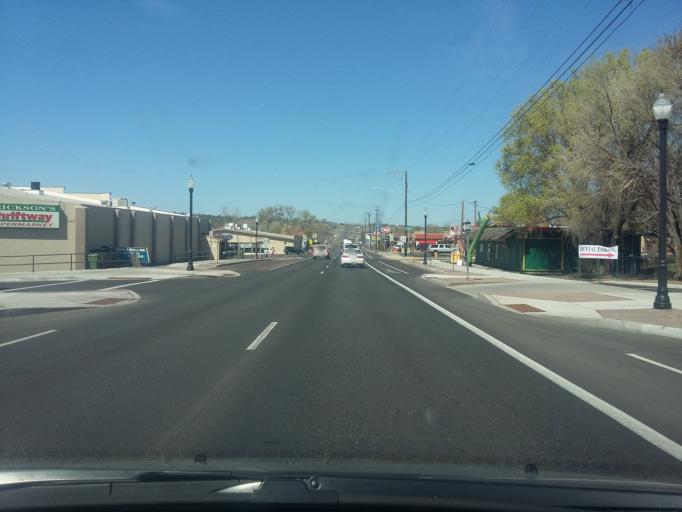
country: US
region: Oregon
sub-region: Jefferson County
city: Madras
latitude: 44.6273
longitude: -121.1296
